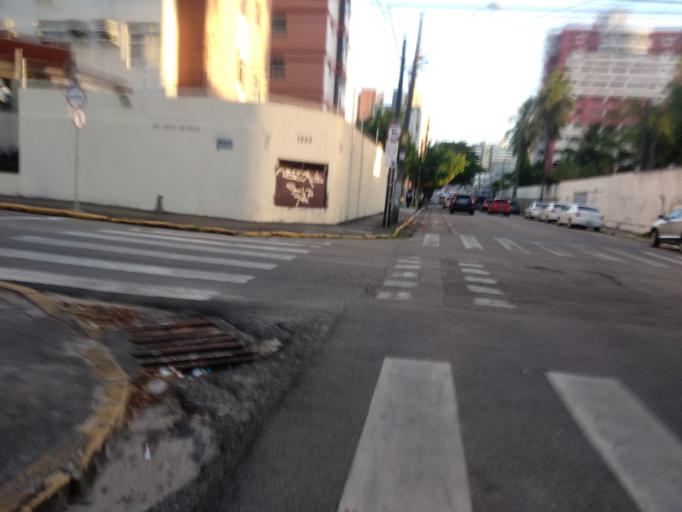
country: BR
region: Ceara
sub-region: Fortaleza
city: Fortaleza
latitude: -3.7369
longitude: -38.5097
